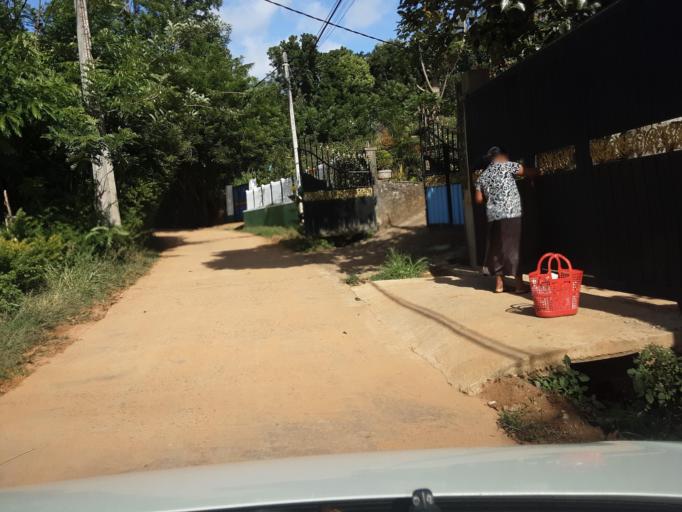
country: LK
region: Uva
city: Haputale
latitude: 6.8944
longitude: 80.9190
